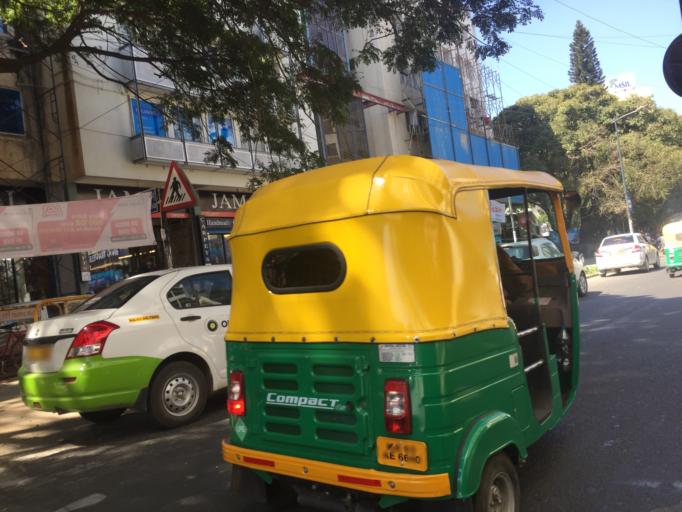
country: IN
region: Karnataka
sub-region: Bangalore Urban
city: Bangalore
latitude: 12.9868
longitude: 77.5950
